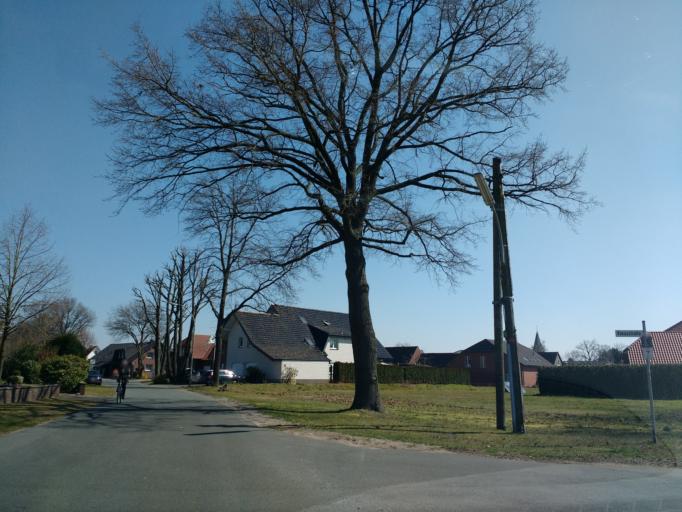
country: DE
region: North Rhine-Westphalia
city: Geseke
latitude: 51.7069
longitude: 8.4804
